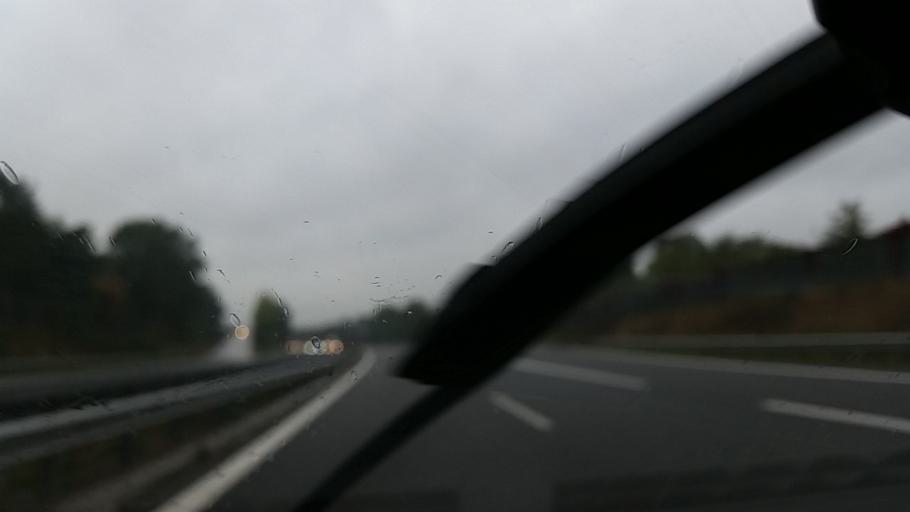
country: DE
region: Hamburg
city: Bergedorf
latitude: 53.4749
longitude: 10.2444
